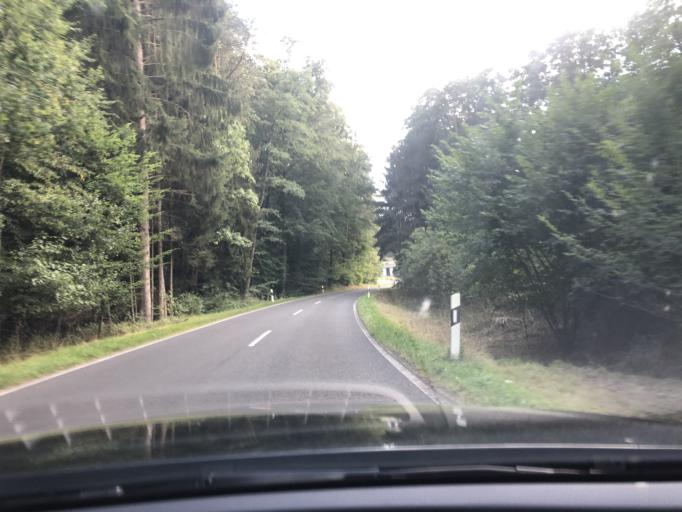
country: DE
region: Bavaria
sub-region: Regierungsbezirk Unterfranken
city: Breitbrunn
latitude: 50.0145
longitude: 10.6771
